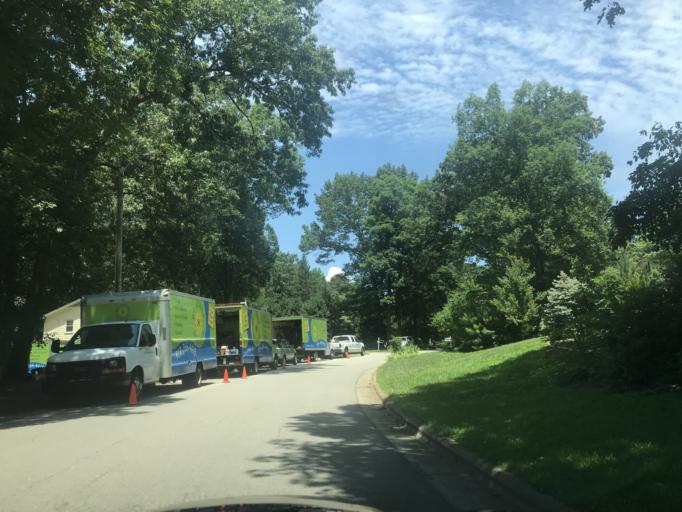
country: US
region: North Carolina
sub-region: Wake County
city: West Raleigh
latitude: 35.8878
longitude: -78.6218
